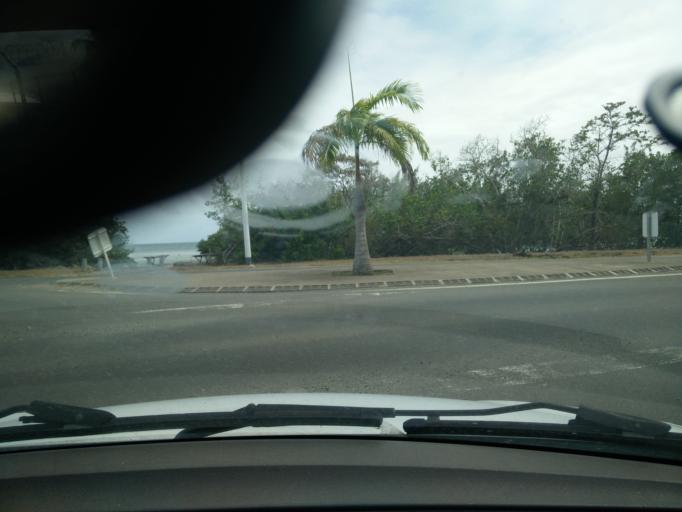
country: GP
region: Guadeloupe
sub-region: Guadeloupe
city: Pointe-a-Pitre
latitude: 16.2243
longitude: -61.5501
